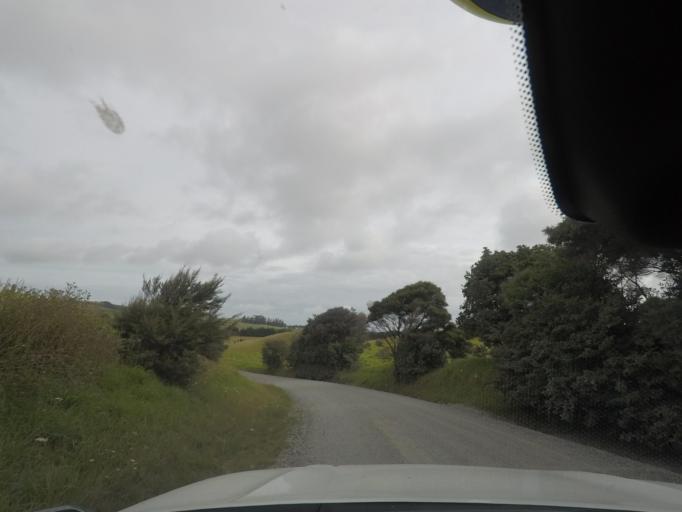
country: NZ
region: Auckland
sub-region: Auckland
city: Parakai
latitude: -36.4740
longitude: 174.2575
